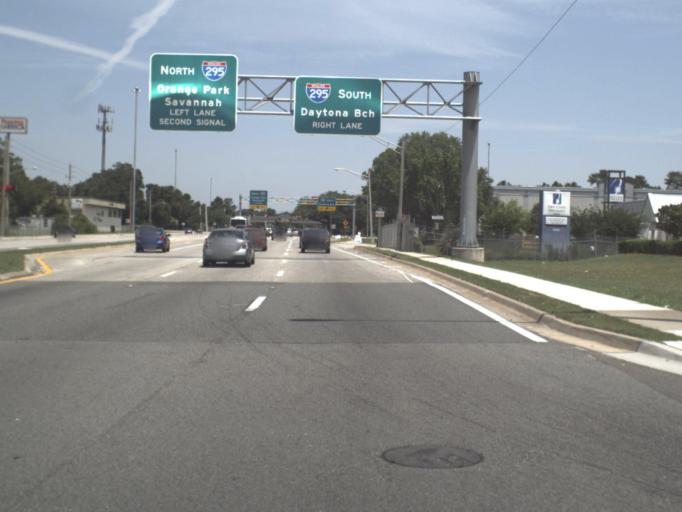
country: US
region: Florida
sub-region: Saint Johns County
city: Fruit Cove
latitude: 30.1772
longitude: -81.6277
